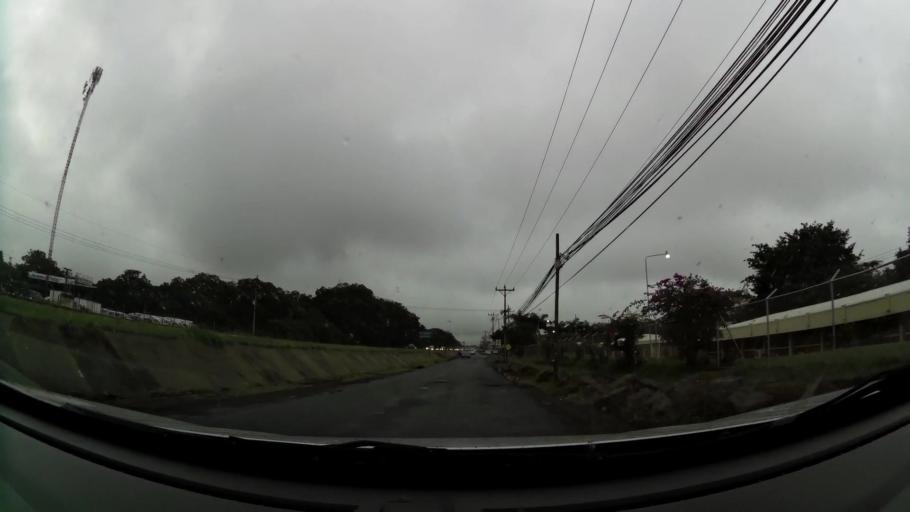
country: CR
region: Alajuela
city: Carrillos
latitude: 9.9956
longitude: -84.2627
